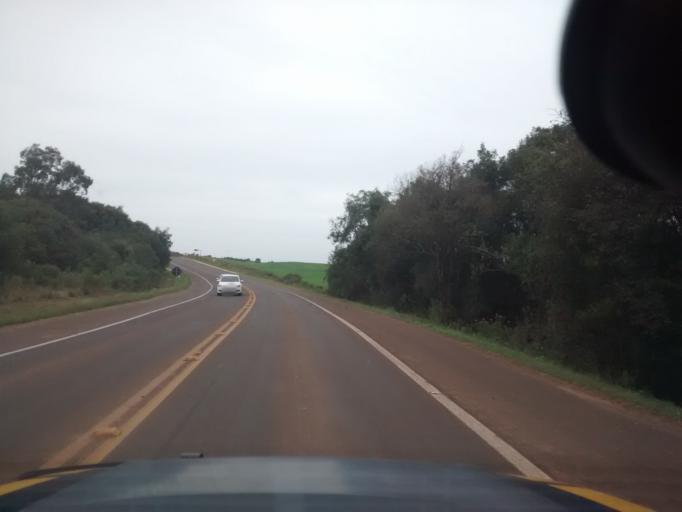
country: BR
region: Rio Grande do Sul
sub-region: Vacaria
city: Vacaria
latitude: -28.4421
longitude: -50.9970
